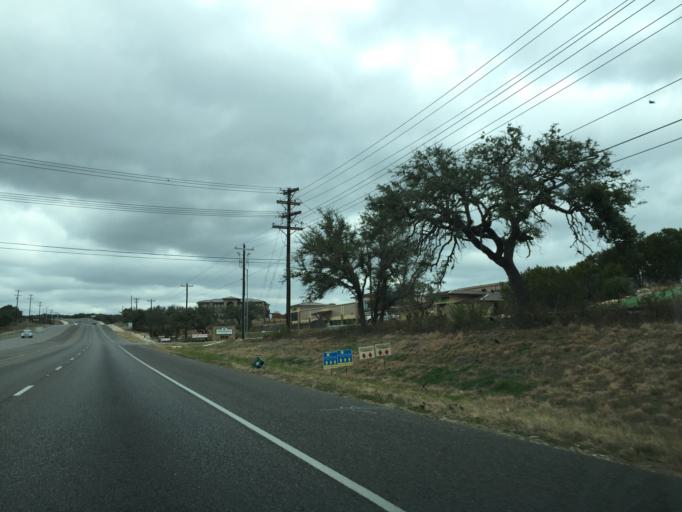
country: US
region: Texas
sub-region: Travis County
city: The Hills
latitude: 30.3418
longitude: -98.0438
